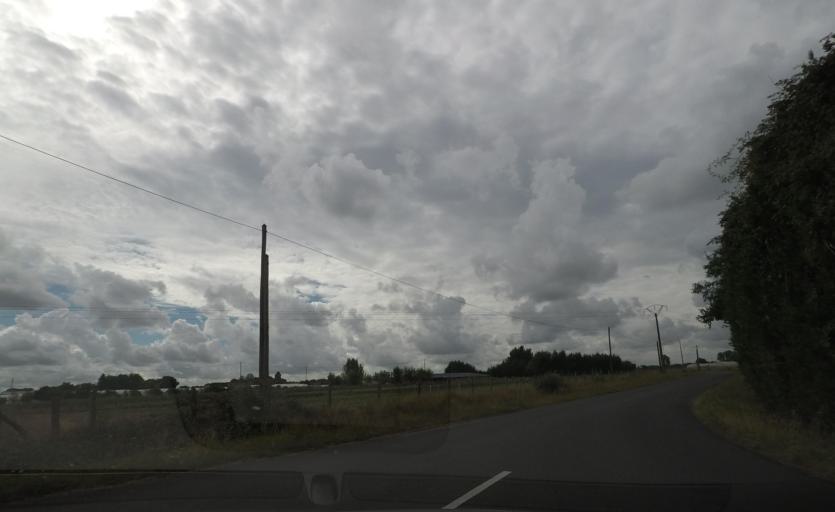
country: FR
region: Pays de la Loire
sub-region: Departement de Maine-et-Loire
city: Corze
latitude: 47.5462
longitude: -0.3932
